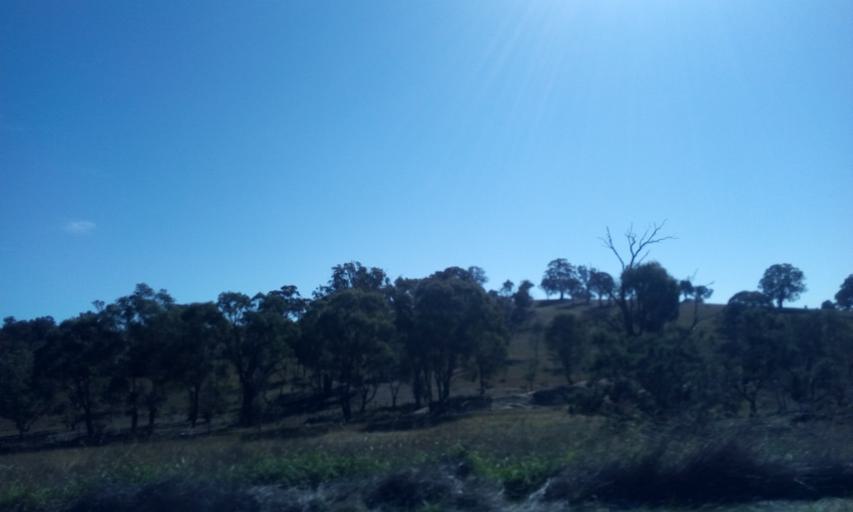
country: AU
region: New South Wales
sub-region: Yass Valley
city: Gundaroo
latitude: -35.1792
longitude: 149.2663
